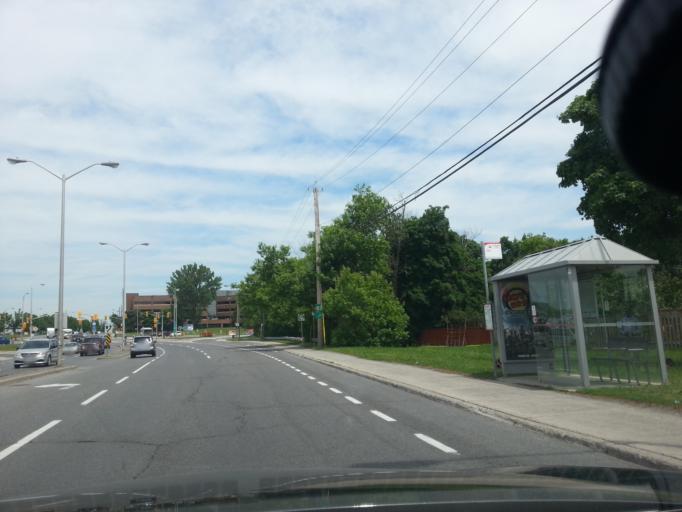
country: CA
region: Ontario
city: Ottawa
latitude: 45.3738
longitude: -75.7081
